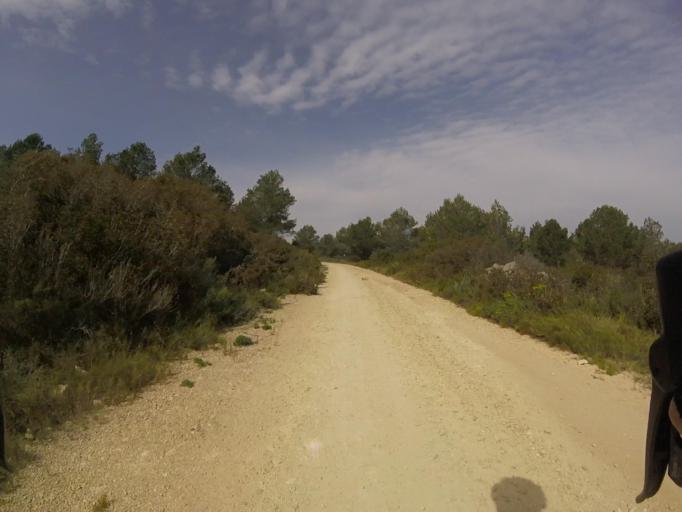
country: ES
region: Valencia
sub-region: Provincia de Castello
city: Cuevas de Vinroma
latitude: 40.2906
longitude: 0.1206
